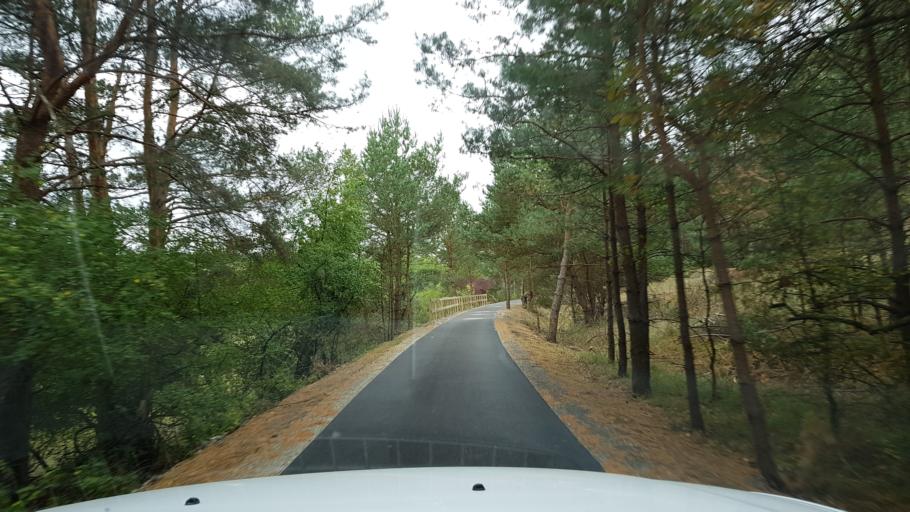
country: PL
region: West Pomeranian Voivodeship
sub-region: Powiat gryfinski
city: Cedynia
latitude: 52.8394
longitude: 14.2858
